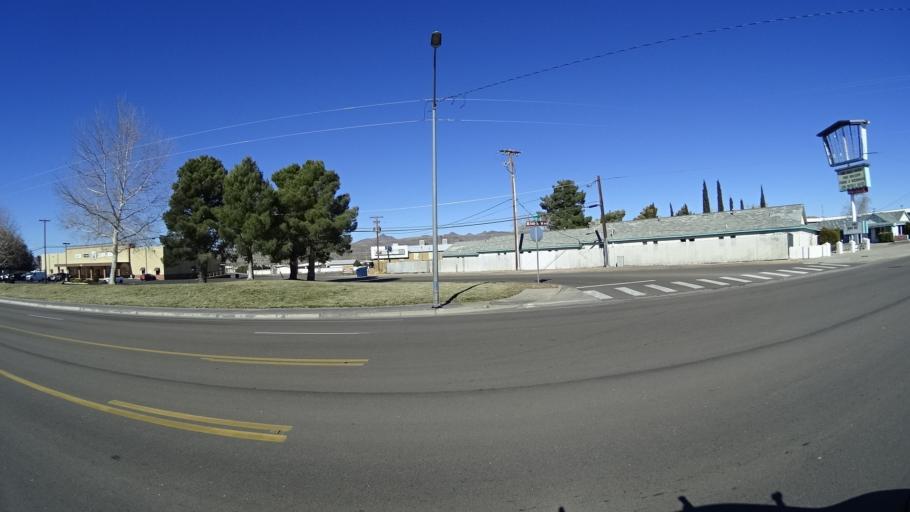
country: US
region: Arizona
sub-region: Mohave County
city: Kingman
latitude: 35.2102
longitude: -114.0171
